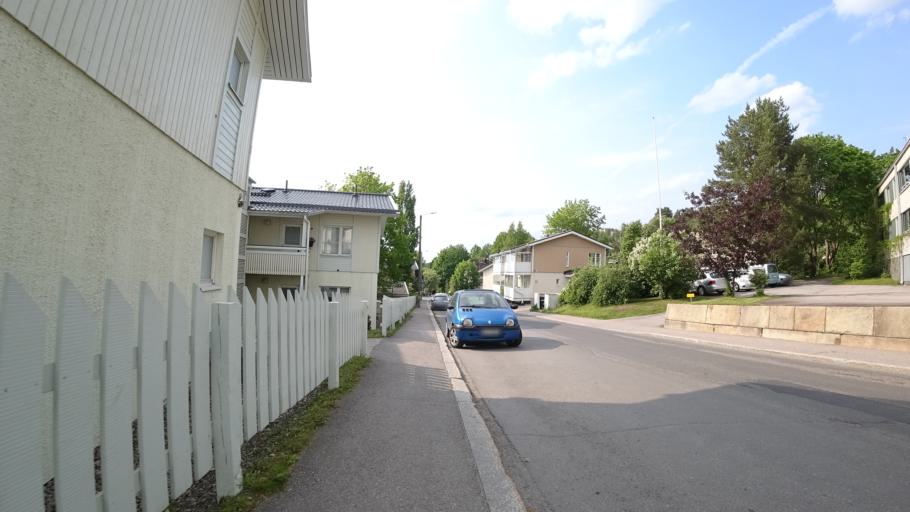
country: FI
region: Pirkanmaa
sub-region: Tampere
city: Tampere
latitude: 61.4985
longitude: 23.7151
